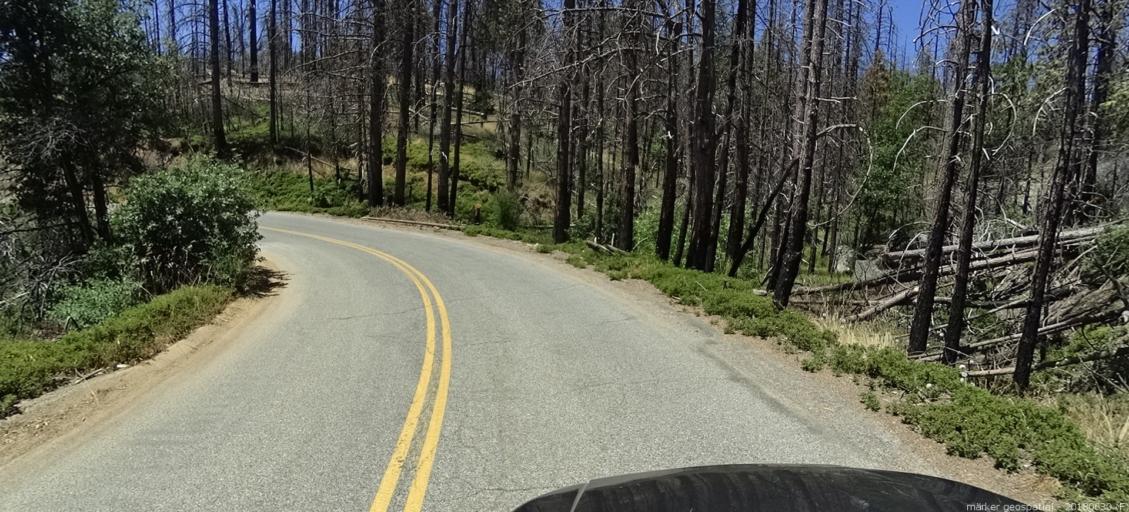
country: US
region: California
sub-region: Fresno County
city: Auberry
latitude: 37.2752
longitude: -119.3577
